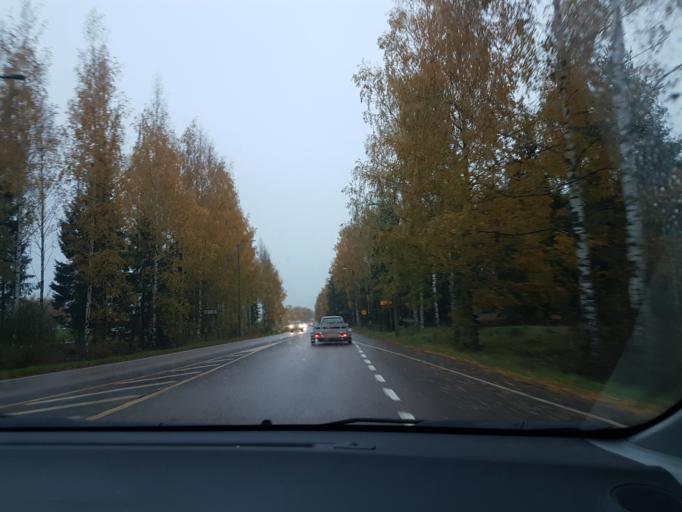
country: FI
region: Uusimaa
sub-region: Helsinki
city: Tuusula
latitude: 60.4045
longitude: 25.0351
